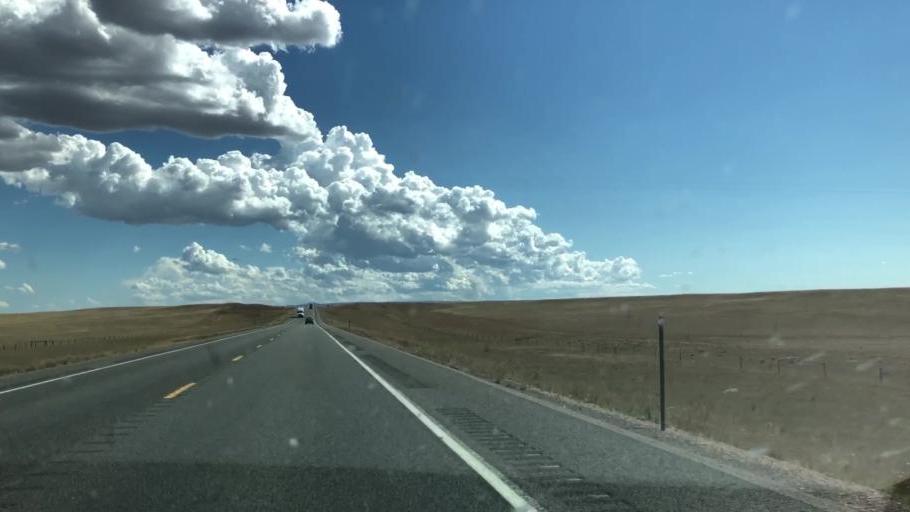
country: US
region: Wyoming
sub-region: Albany County
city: Laramie
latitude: 41.2317
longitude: -105.6007
